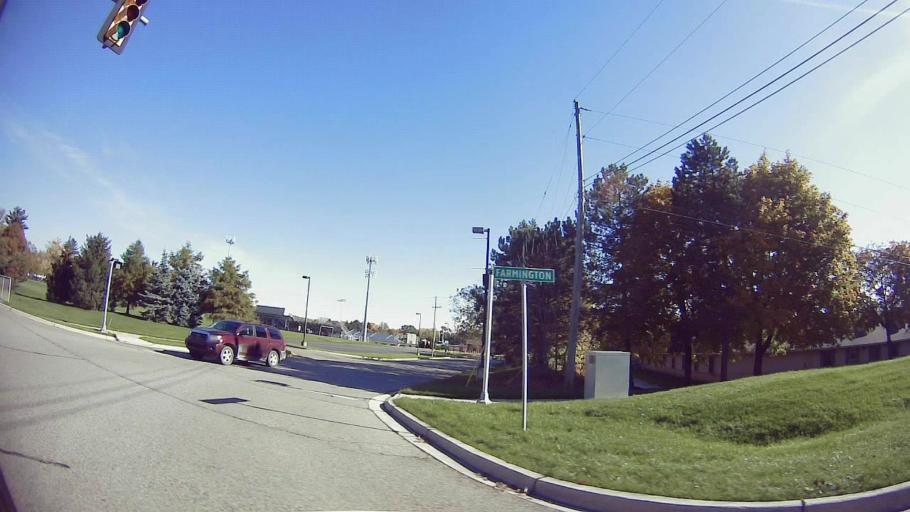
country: US
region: Michigan
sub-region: Oakland County
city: Farmington Hills
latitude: 42.5163
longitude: -83.3790
